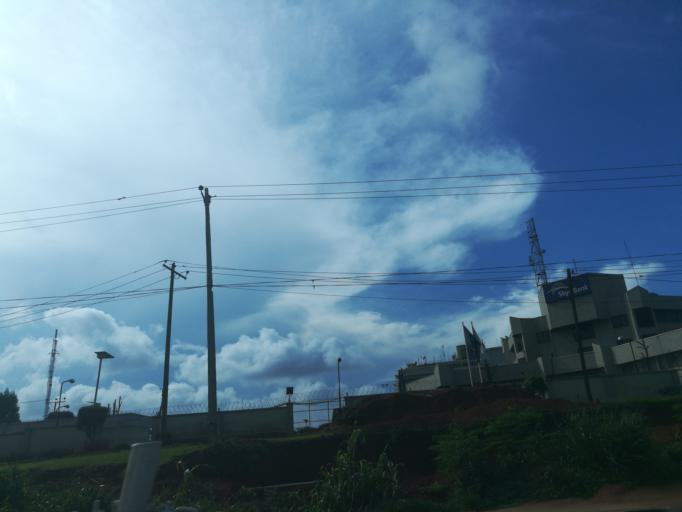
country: NG
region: Lagos
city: Ikeja
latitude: 6.6156
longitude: 3.3574
